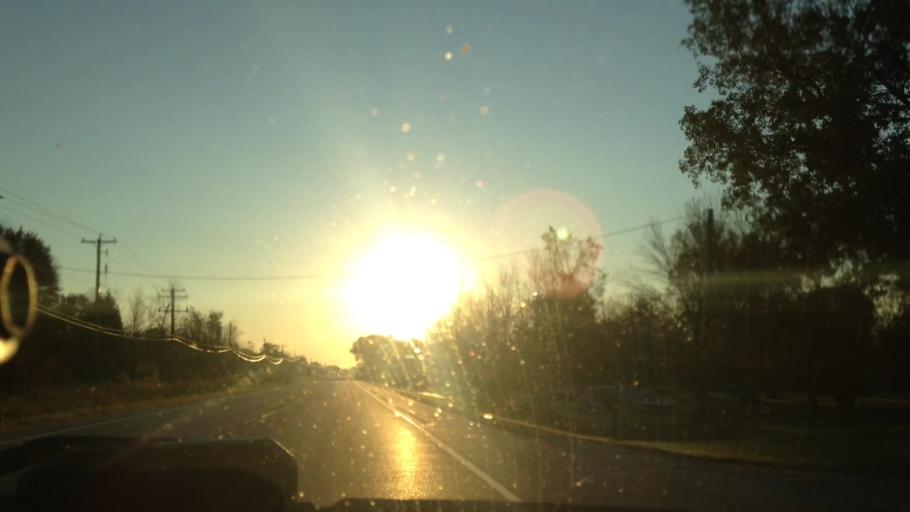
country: US
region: Wisconsin
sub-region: Washington County
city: Newburg
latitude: 43.4253
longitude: -88.1123
